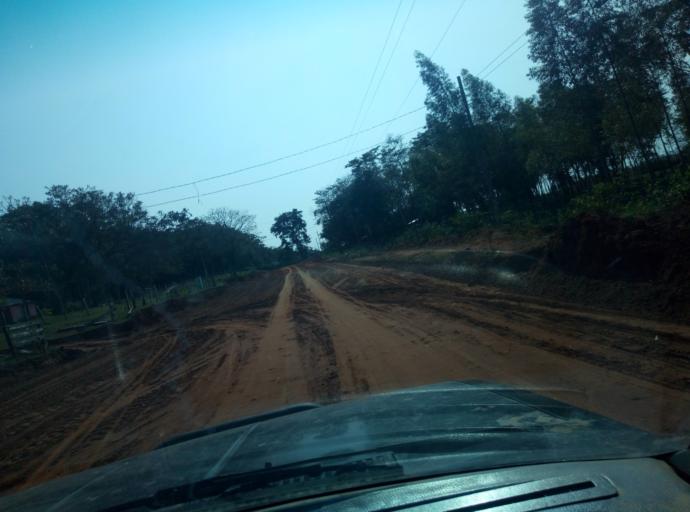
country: PY
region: Caaguazu
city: Carayao
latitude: -25.3074
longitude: -56.3251
